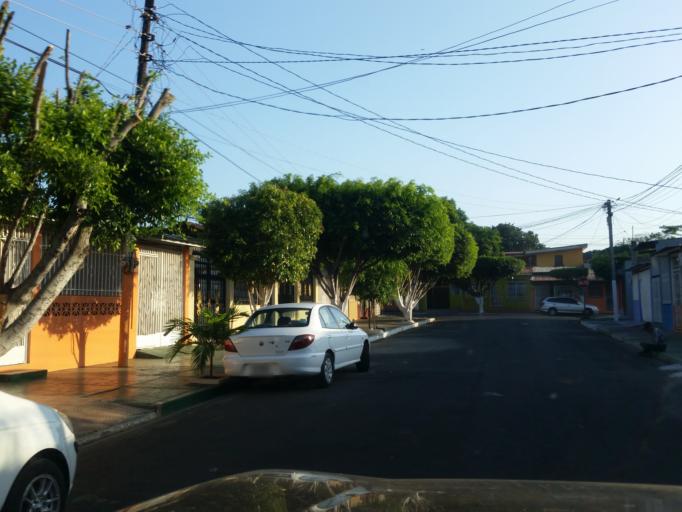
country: NI
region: Managua
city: Ciudad Sandino
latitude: 12.1485
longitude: -86.3029
